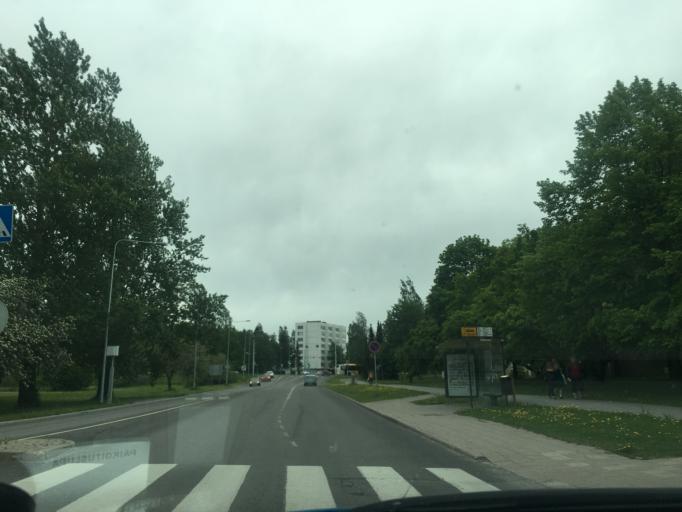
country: FI
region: Varsinais-Suomi
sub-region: Turku
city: Turku
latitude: 60.4600
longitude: 22.3070
